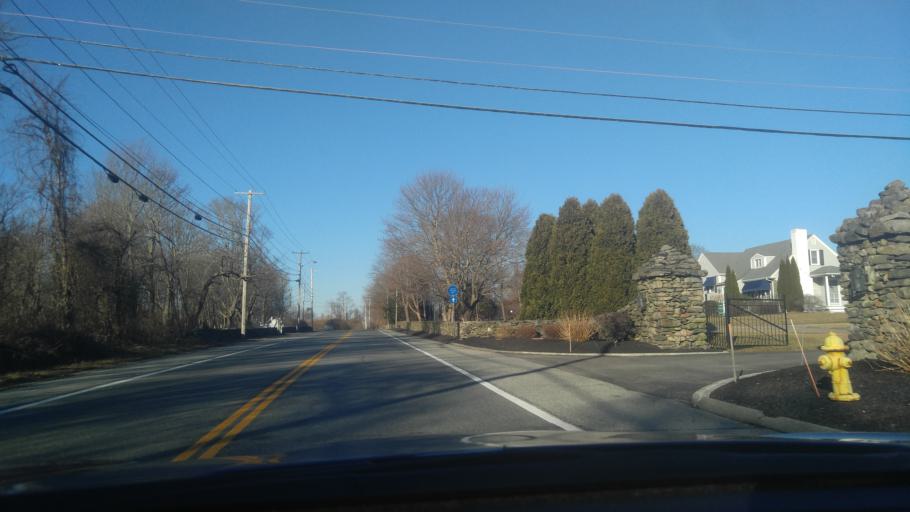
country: US
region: Rhode Island
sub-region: Washington County
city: Narragansett Pier
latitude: 41.4611
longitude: -71.4337
